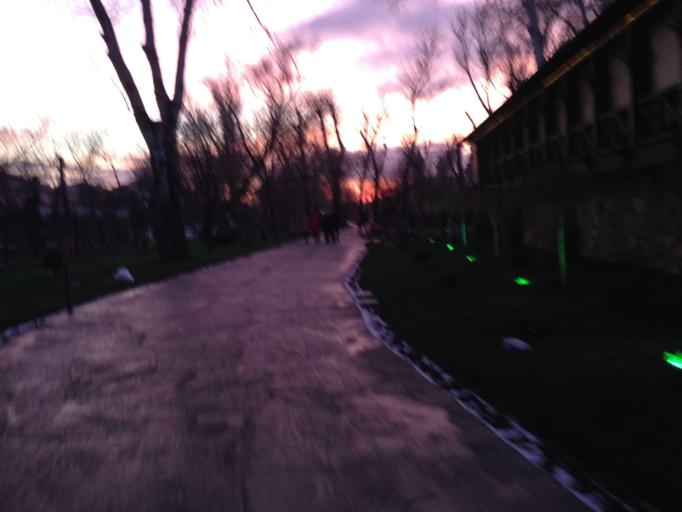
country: RU
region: Rostov
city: Staraya Stanitsa
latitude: 48.3519
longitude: 40.2956
